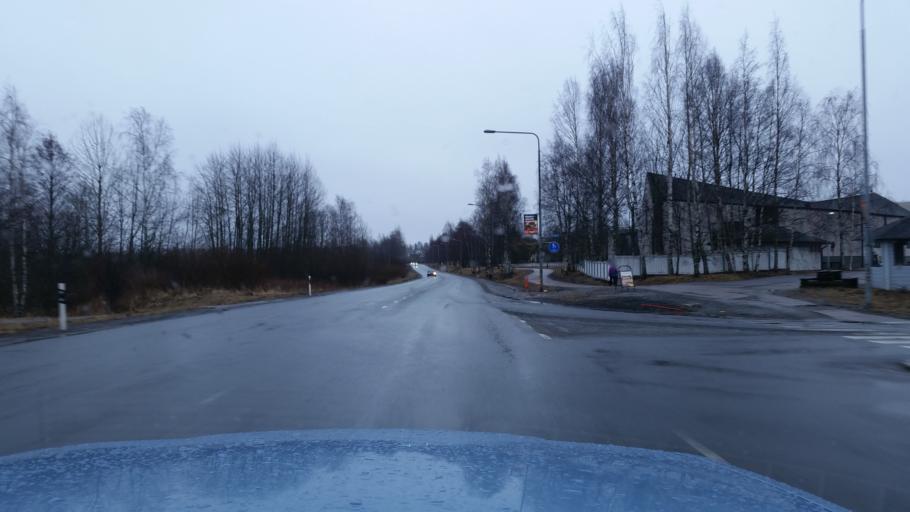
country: FI
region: Pirkanmaa
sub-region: Tampere
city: Tampere
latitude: 61.4831
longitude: 23.8029
